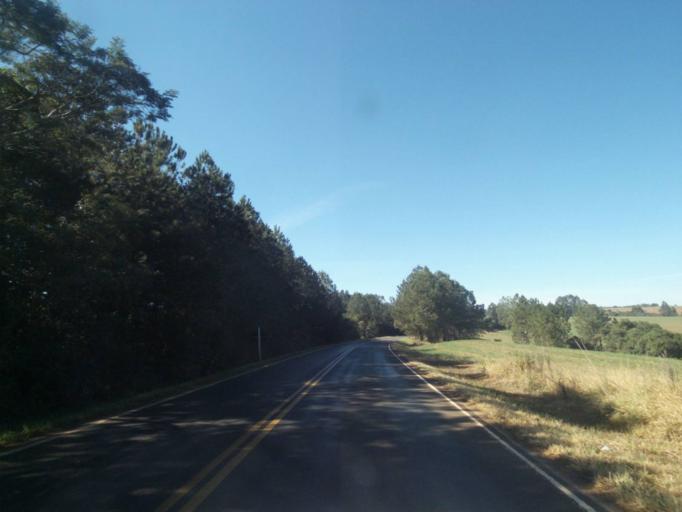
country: BR
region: Parana
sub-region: Tibagi
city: Tibagi
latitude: -24.4931
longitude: -50.4640
